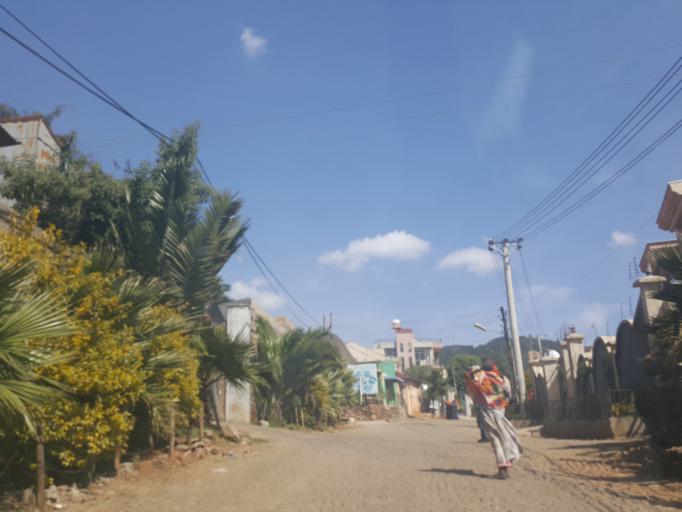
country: ET
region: Adis Abeba
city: Addis Ababa
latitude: 9.0693
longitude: 38.7158
